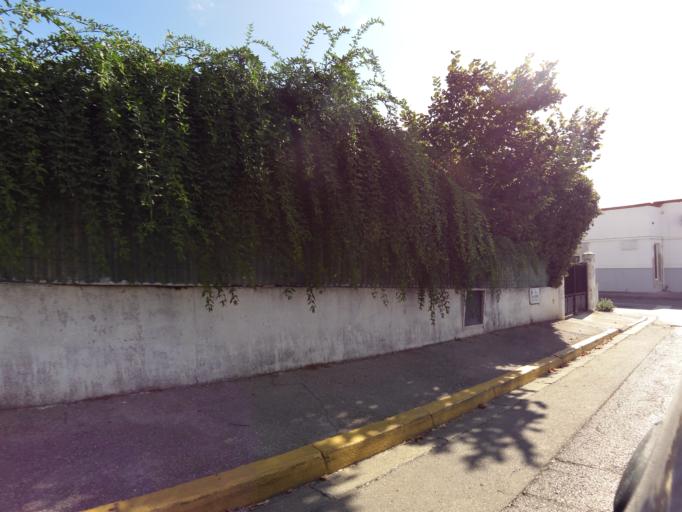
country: FR
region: Languedoc-Roussillon
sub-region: Departement de l'Herault
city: Lunel
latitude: 43.6776
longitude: 4.1406
